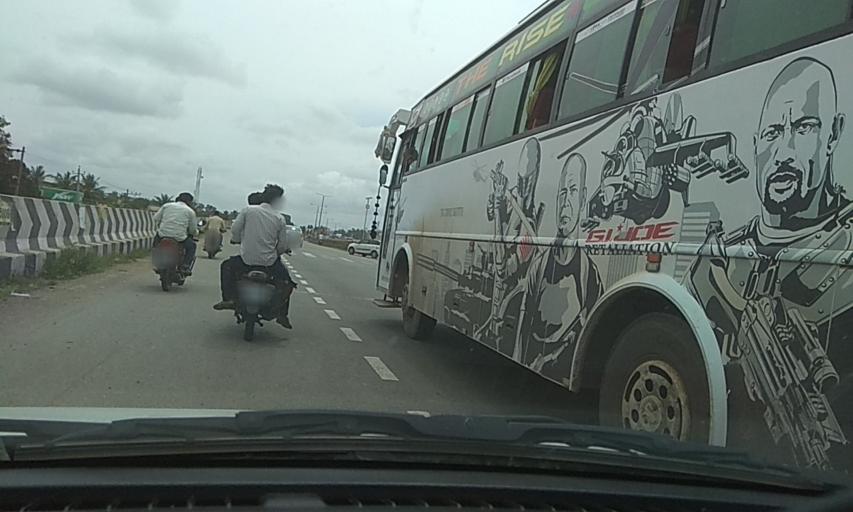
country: IN
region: Karnataka
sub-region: Chitradurga
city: Chitradurga
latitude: 14.2383
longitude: 76.3787
